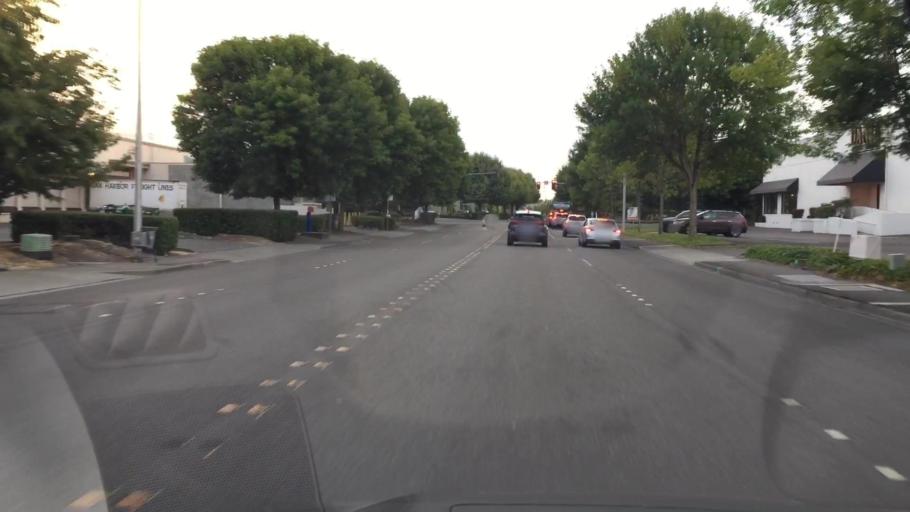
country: US
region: Washington
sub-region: King County
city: Tukwila
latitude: 47.4426
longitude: -122.2546
